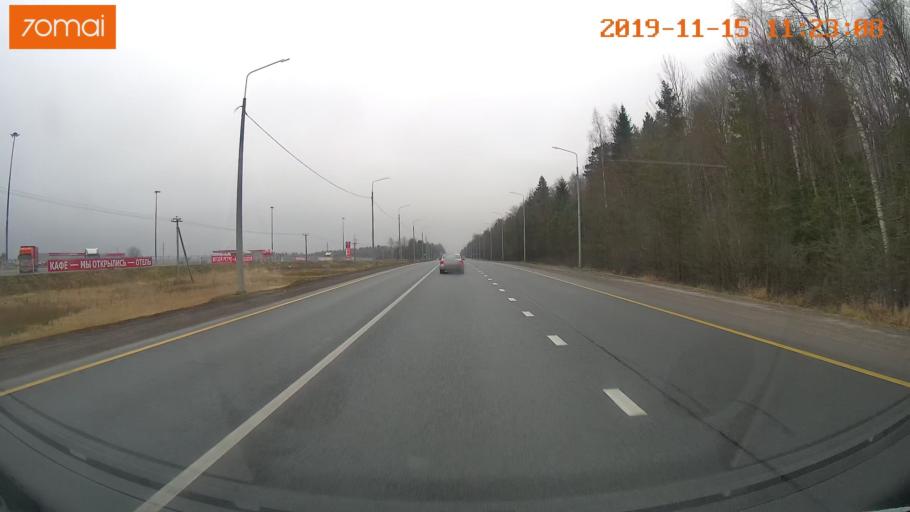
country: RU
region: Vologda
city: Molochnoye
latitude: 59.1498
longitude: 39.3751
